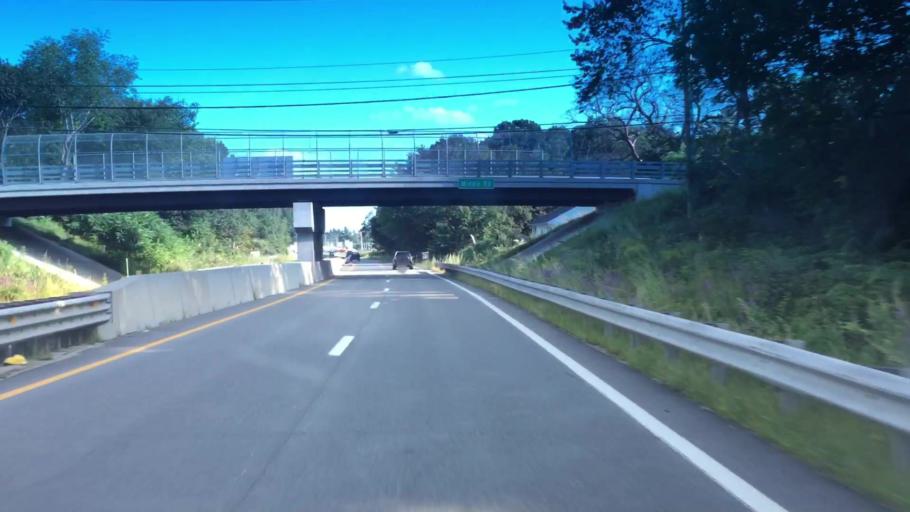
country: US
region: New Hampshire
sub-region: Rockingham County
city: Portsmouth
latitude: 43.0643
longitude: -70.7758
